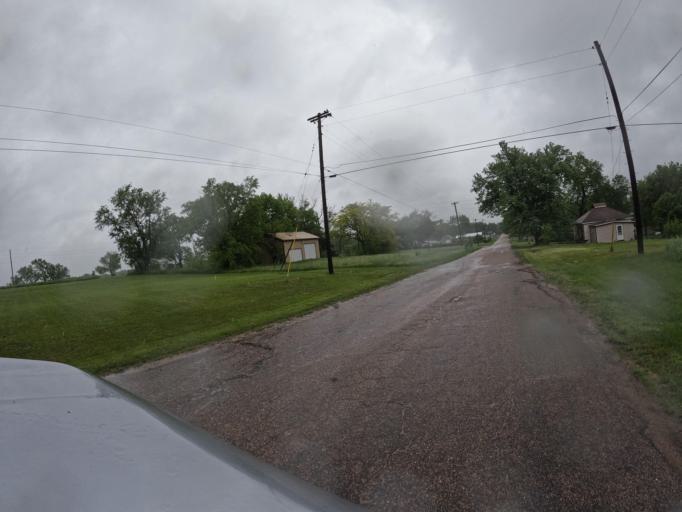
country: US
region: Nebraska
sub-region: Gage County
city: Wymore
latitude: 40.1260
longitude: -96.6559
